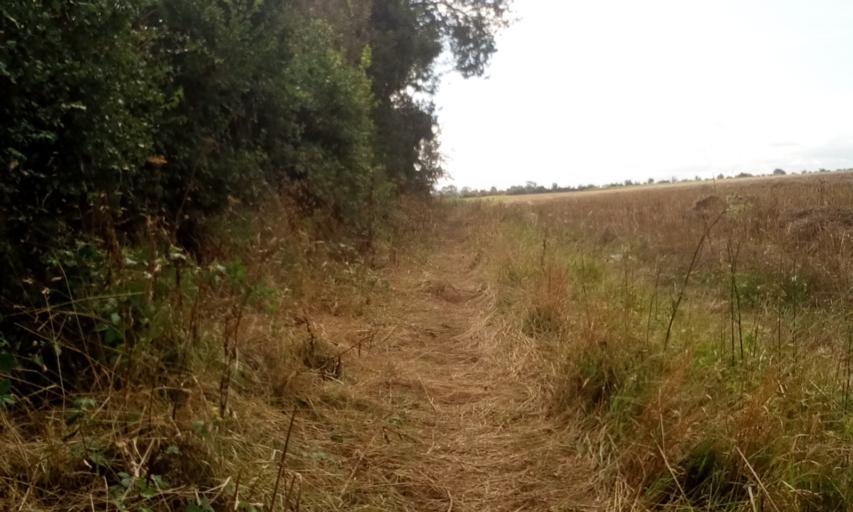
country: FR
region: Lower Normandy
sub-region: Departement du Calvados
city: Cheux
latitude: 49.2030
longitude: -0.5455
